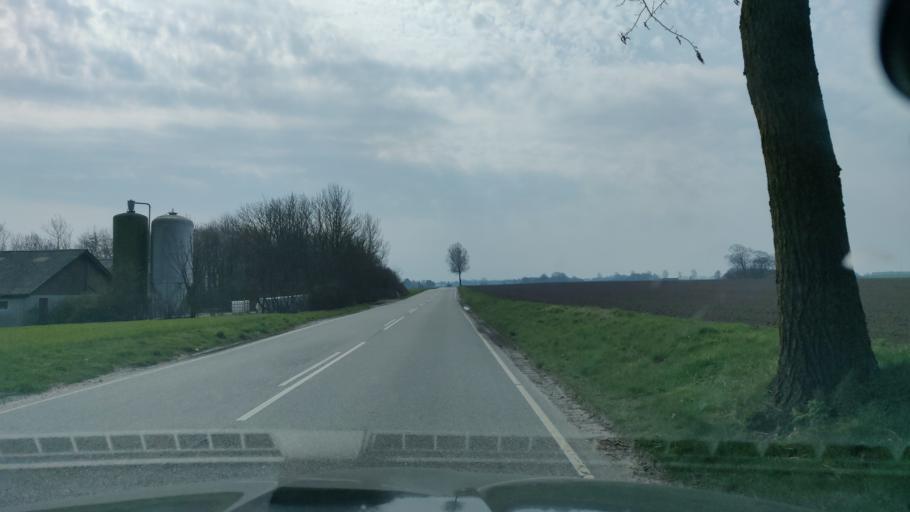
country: DK
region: South Denmark
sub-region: Nordfyns Kommune
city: Sonderso
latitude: 55.5092
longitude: 10.2498
